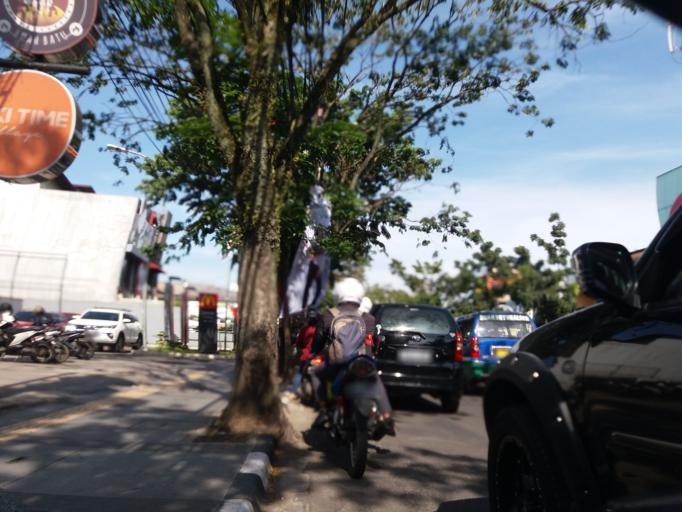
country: ID
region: West Java
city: Bandung
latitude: -6.9390
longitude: 107.6248
